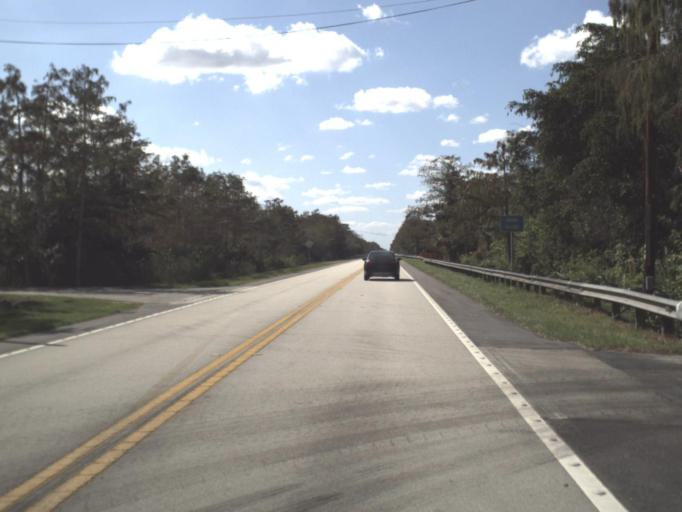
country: US
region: Florida
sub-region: Miami-Dade County
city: Kendall West
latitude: 25.8464
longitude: -80.9287
